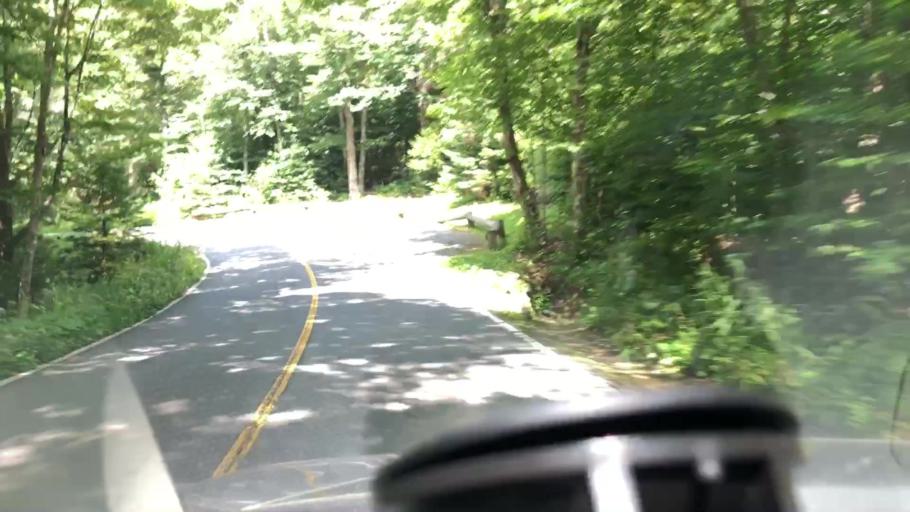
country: US
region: Massachusetts
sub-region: Berkshire County
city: Adams
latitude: 42.6628
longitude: -73.1609
